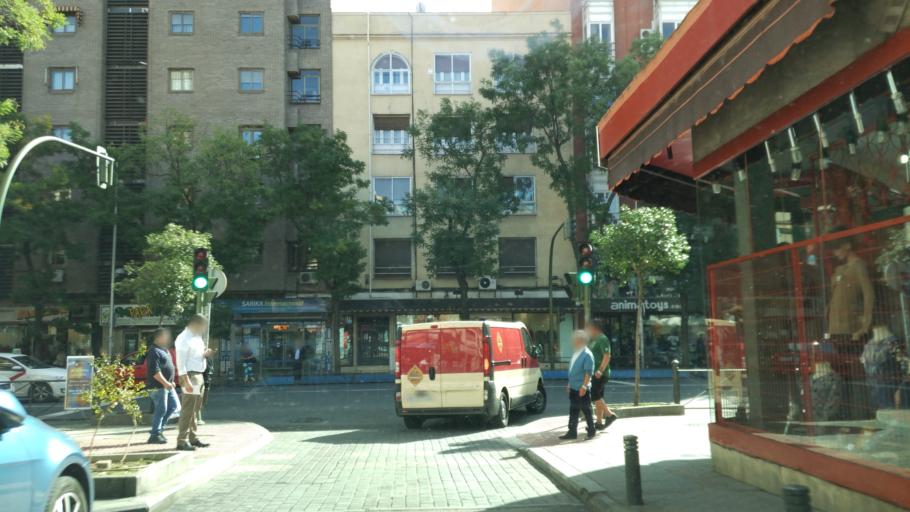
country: ES
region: Madrid
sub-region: Provincia de Madrid
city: Tetuan de las Victorias
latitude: 40.4590
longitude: -3.7006
